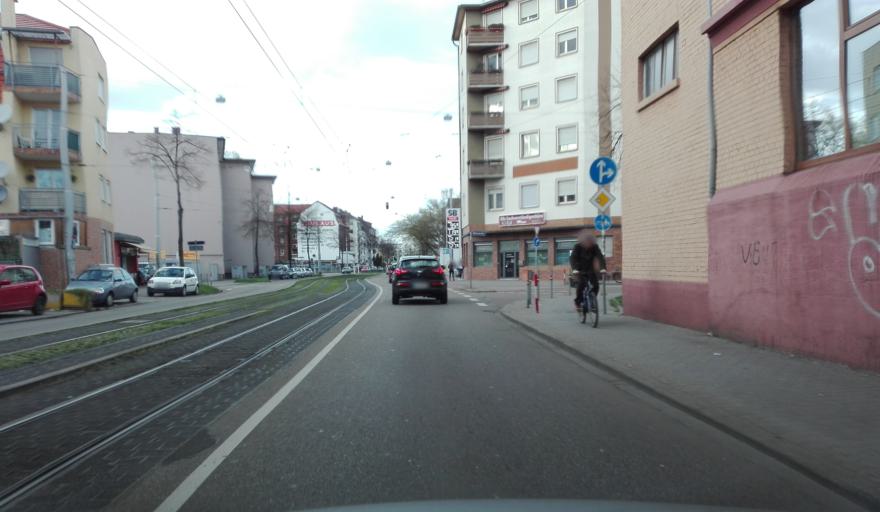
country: DE
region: Baden-Wuerttemberg
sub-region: Karlsruhe Region
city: Mannheim
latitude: 49.5016
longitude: 8.4709
